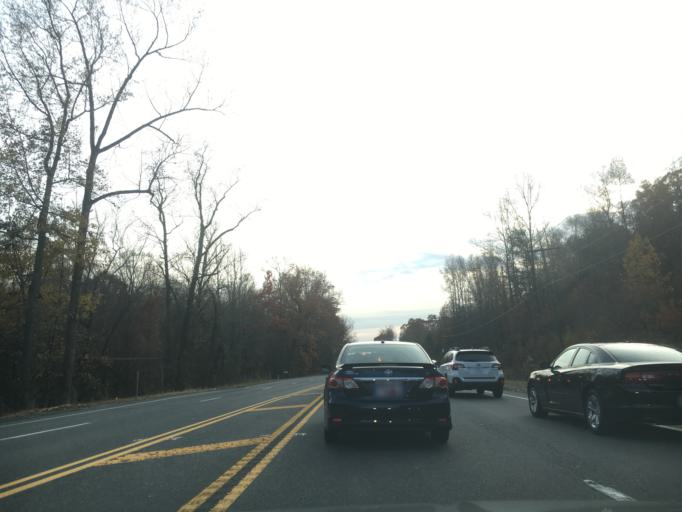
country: US
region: Virginia
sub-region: Stafford County
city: Aquia Harbour
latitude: 38.4900
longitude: -77.3823
